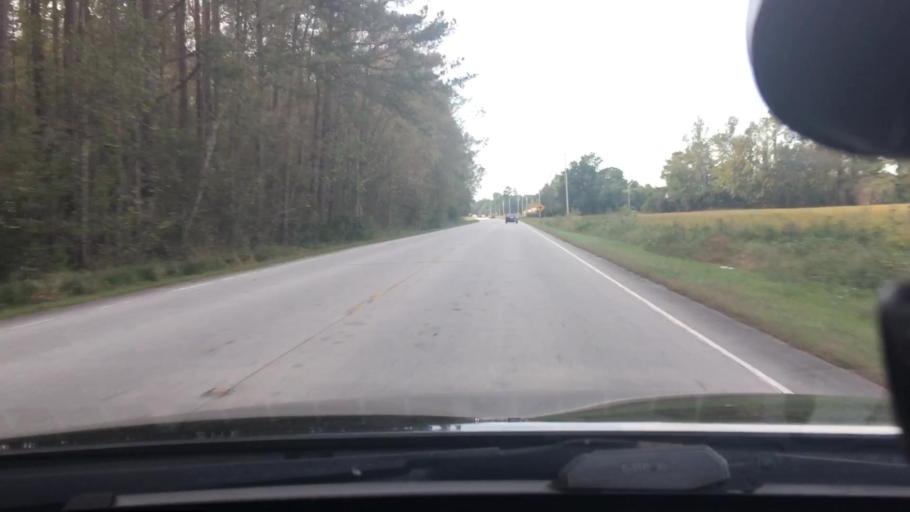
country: US
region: North Carolina
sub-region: Craven County
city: Vanceboro
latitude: 35.3983
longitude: -77.2362
